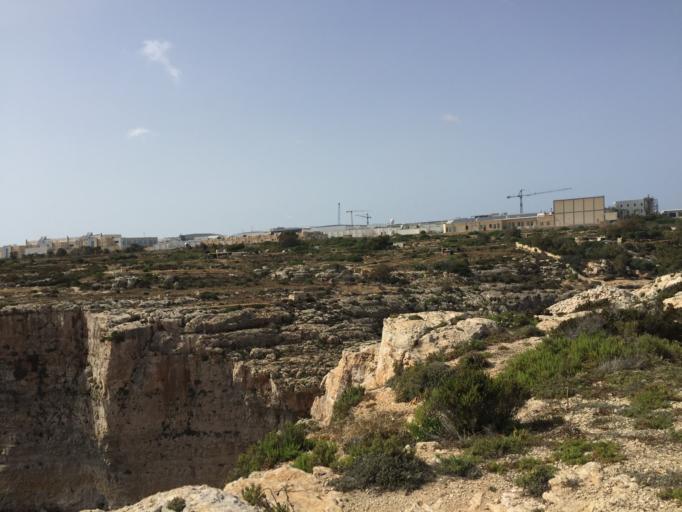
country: MT
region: Birzebbuga
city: Birzebbuga
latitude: 35.8077
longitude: 14.5107
